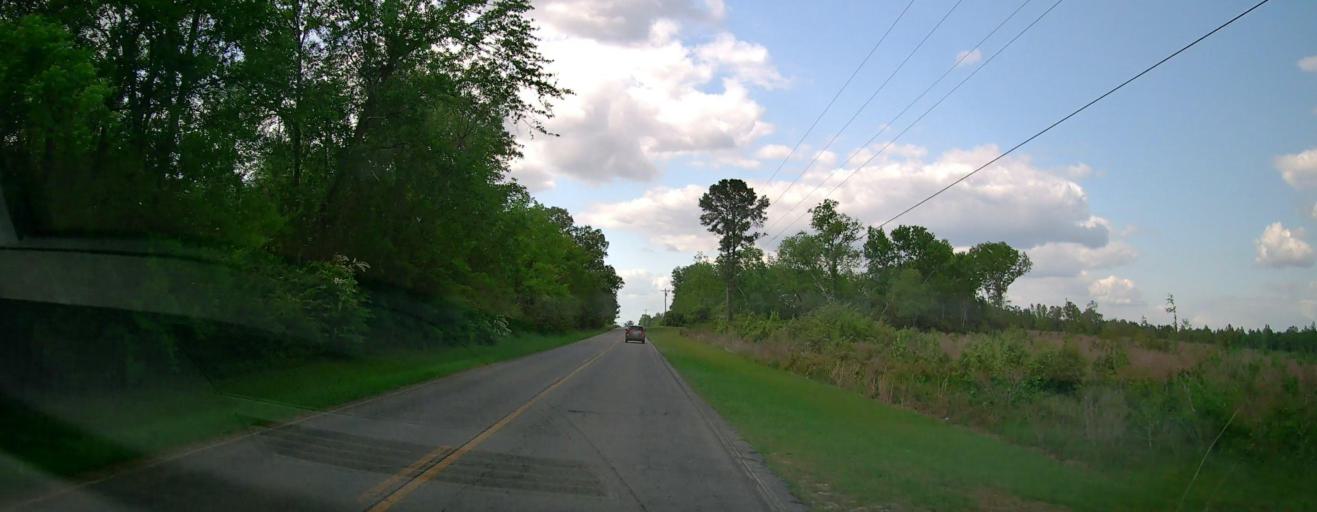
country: US
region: Georgia
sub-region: Laurens County
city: East Dublin
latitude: 32.5970
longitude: -82.8658
